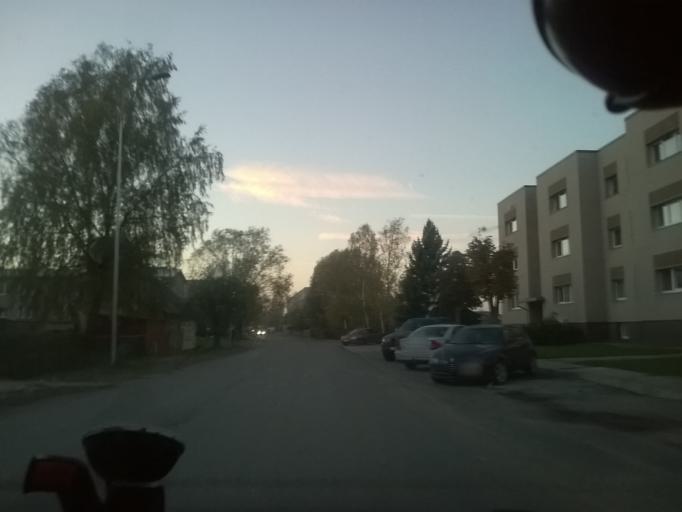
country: EE
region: Laeaene
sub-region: Haapsalu linn
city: Haapsalu
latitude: 58.9409
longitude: 23.5510
